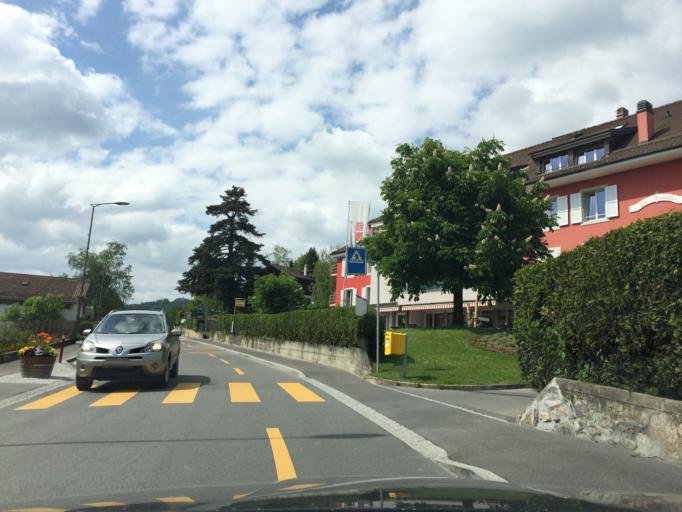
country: CH
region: Vaud
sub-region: Lavaux-Oron District
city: Chexbres
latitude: 46.4845
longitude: 6.7742
